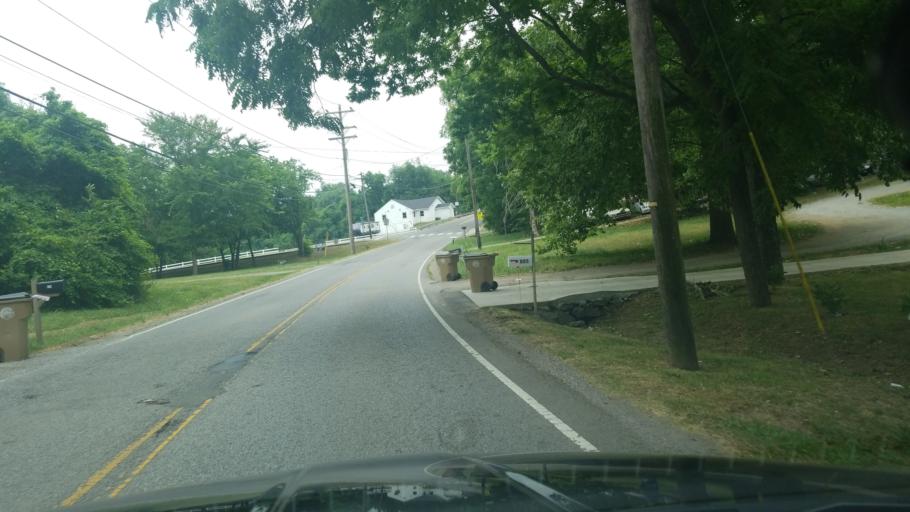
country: US
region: Tennessee
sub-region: Davidson County
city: Goodlettsville
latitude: 36.2546
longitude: -86.7448
